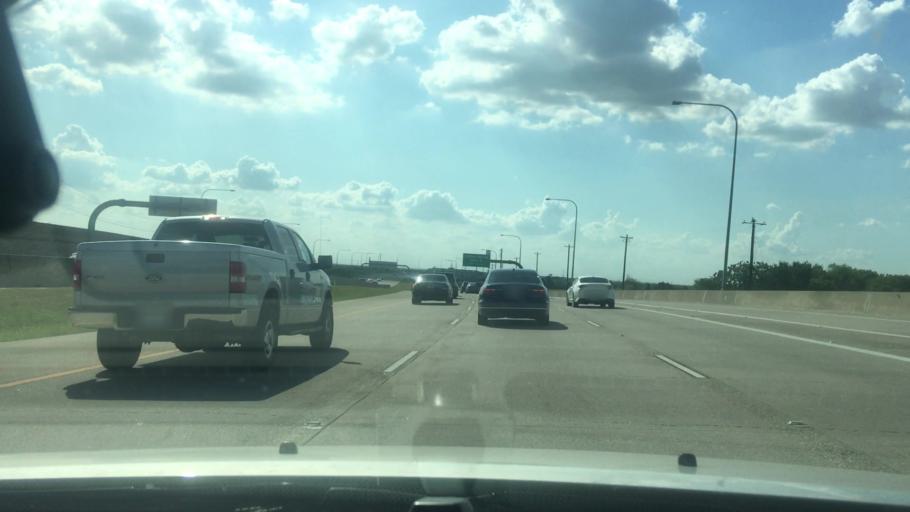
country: US
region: Texas
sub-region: Collin County
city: Frisco
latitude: 33.1349
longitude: -96.8287
